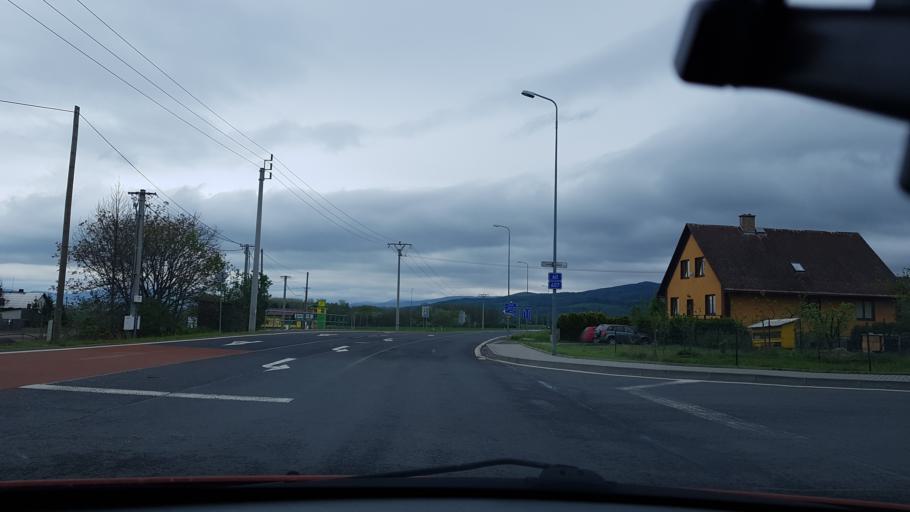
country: CZ
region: Olomoucky
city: Javornik
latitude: 50.3944
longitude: 17.0129
